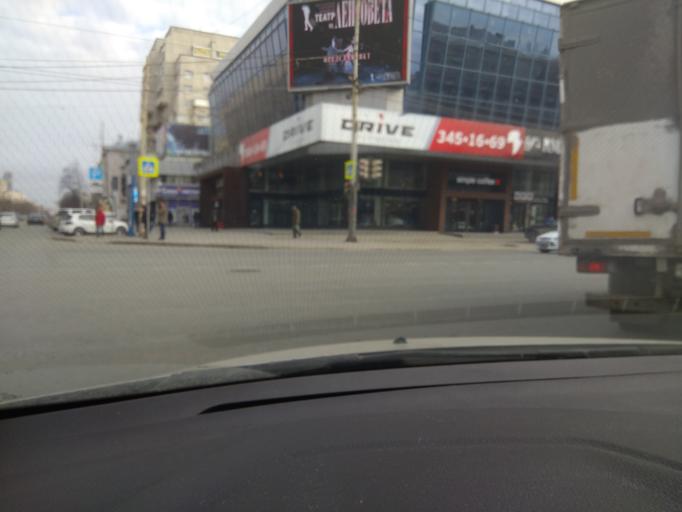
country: RU
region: Sverdlovsk
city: Yekaterinburg
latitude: 56.8361
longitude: 60.6221
